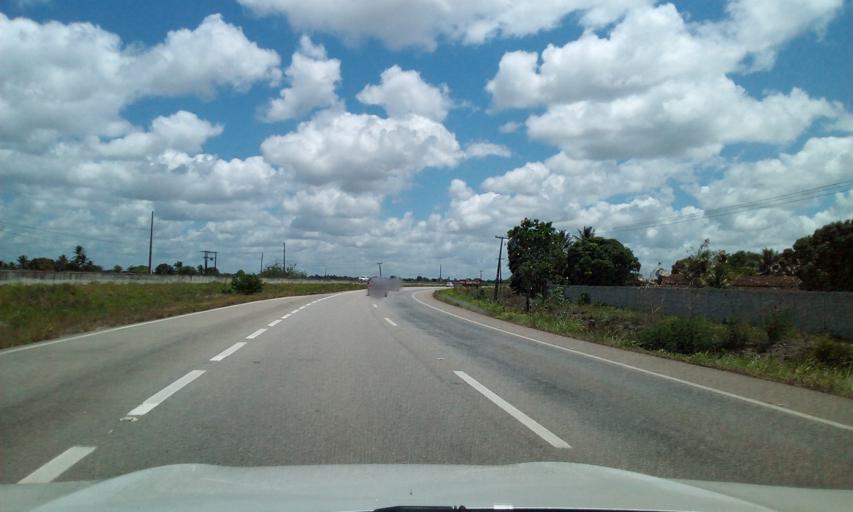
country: BR
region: Alagoas
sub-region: Junqueiro
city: Junqueiro
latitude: -9.8870
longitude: -36.3892
